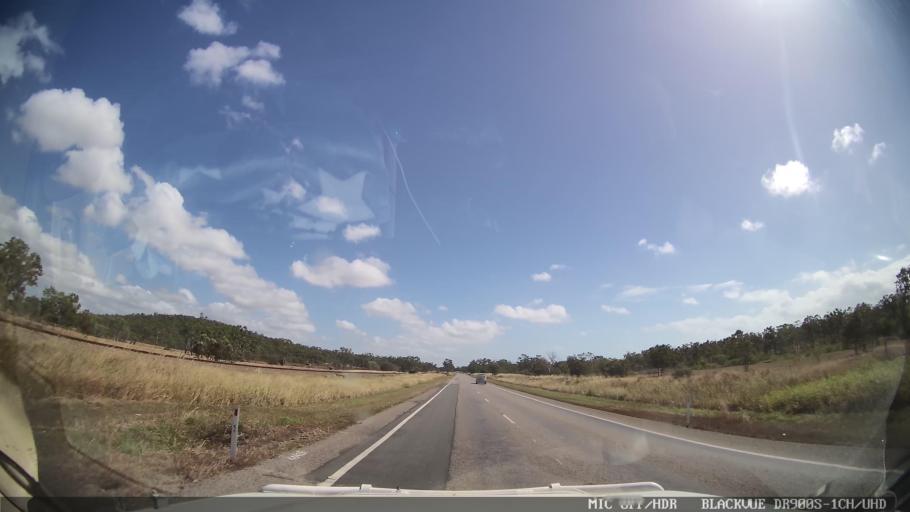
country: AU
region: Queensland
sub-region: Whitsunday
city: Red Hill
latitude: -20.1827
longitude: 148.3529
